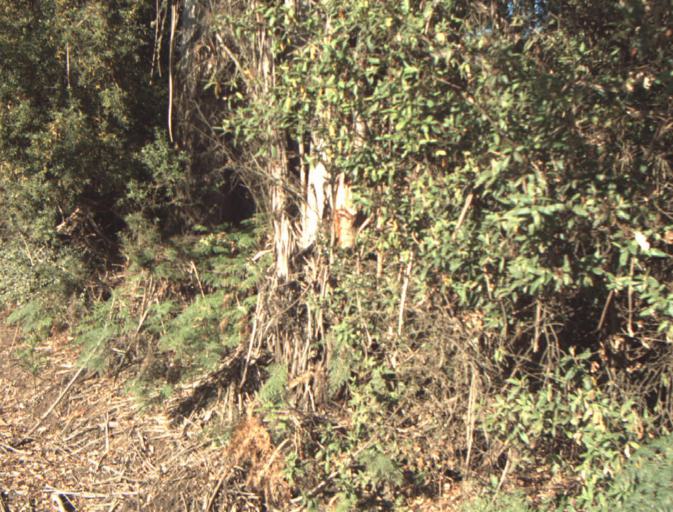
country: AU
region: Tasmania
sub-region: Launceston
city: Mayfield
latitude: -41.3020
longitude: 147.1983
